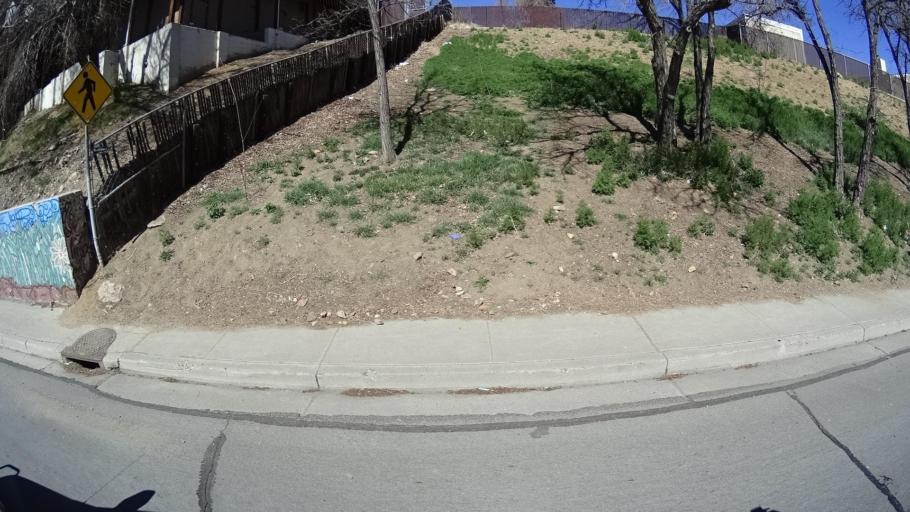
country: US
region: Nevada
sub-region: Washoe County
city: Reno
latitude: 39.5523
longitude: -119.7927
